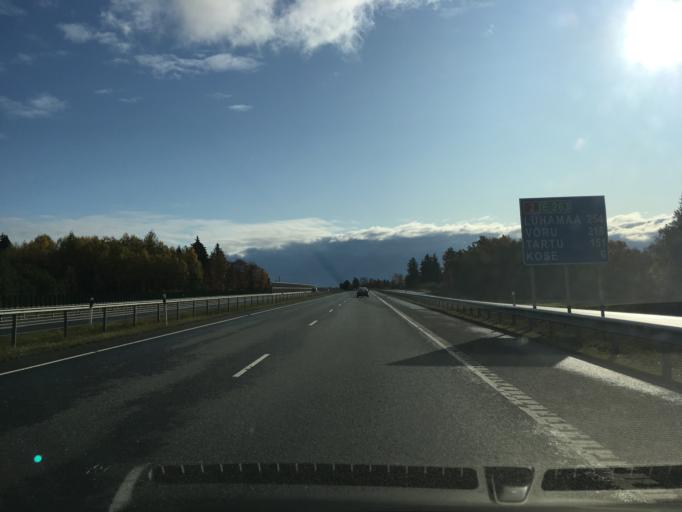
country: EE
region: Harju
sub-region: Rae vald
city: Vaida
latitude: 59.1858
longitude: 25.0677
